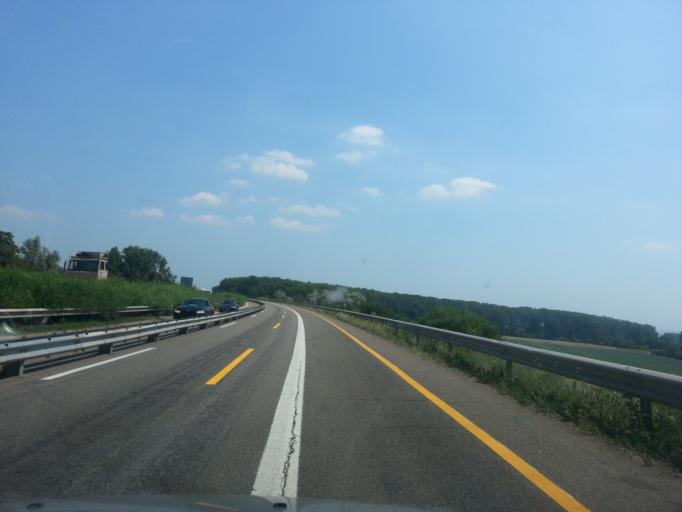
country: DE
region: Rheinland-Pfalz
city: Frankenthal
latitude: 49.5457
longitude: 8.4066
